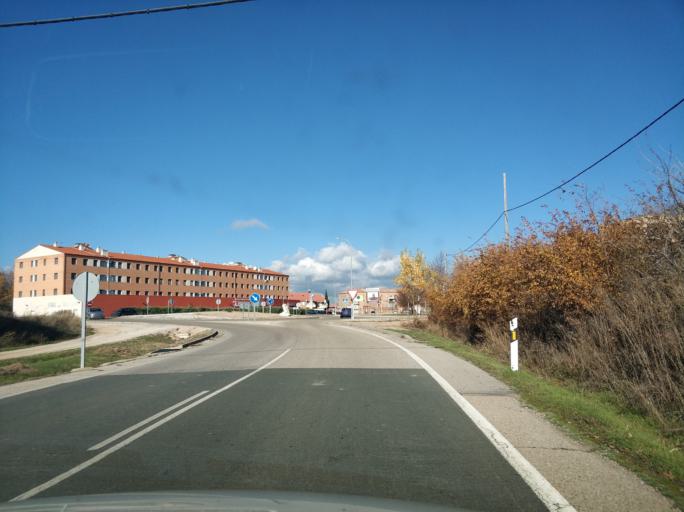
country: ES
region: Castille and Leon
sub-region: Provincia de Soria
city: Almazan
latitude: 41.4788
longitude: -2.5293
